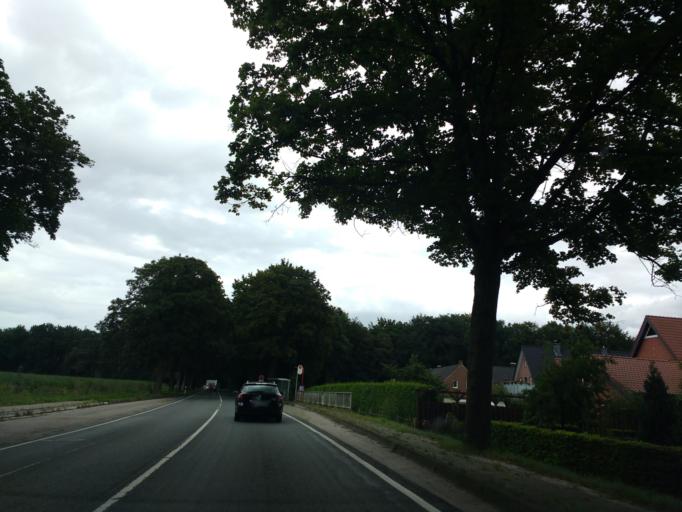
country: DE
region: Lower Saxony
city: Glandorf
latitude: 52.0877
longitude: 8.0344
